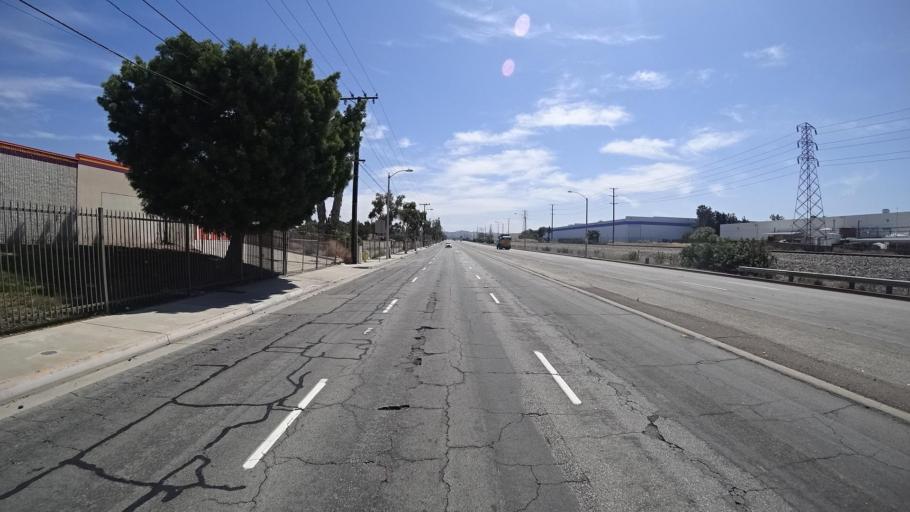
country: US
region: California
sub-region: Los Angeles County
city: South San Jose Hills
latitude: 34.0041
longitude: -117.8943
